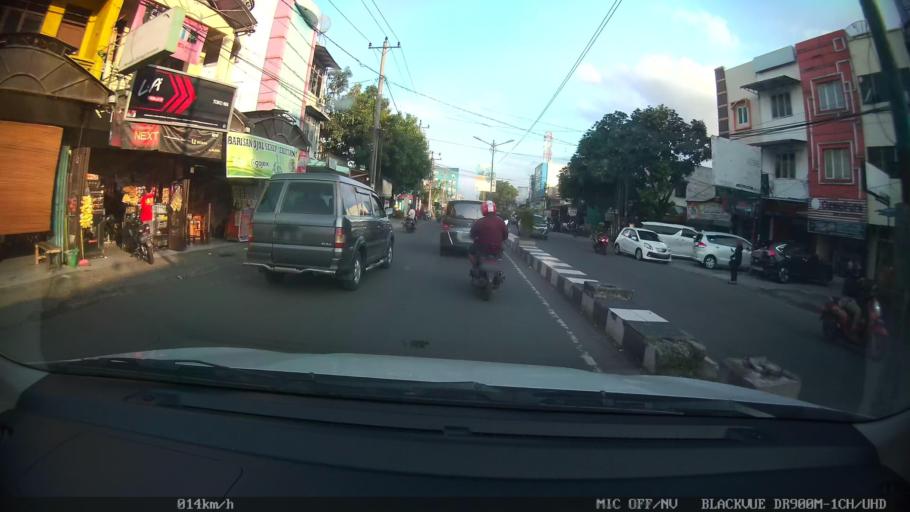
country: ID
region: North Sumatra
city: Medan
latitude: 3.5983
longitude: 98.6639
